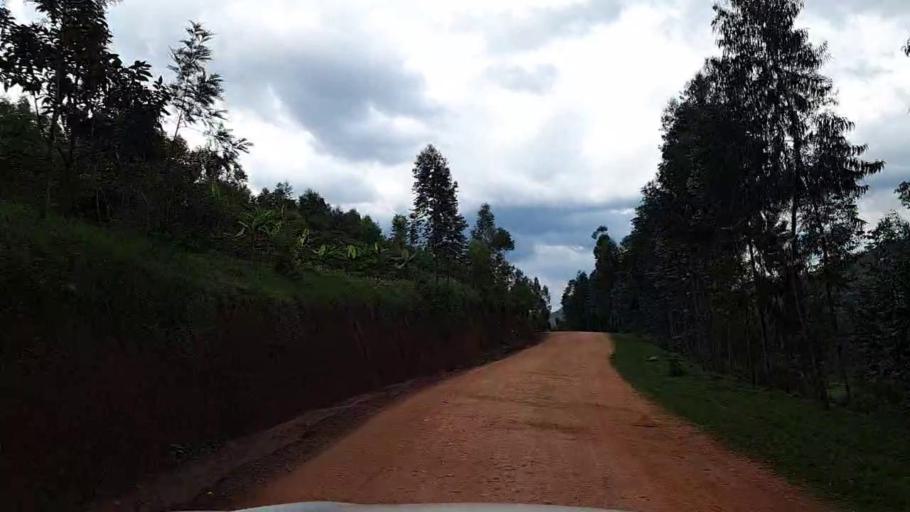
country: RW
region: Southern Province
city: Nyanza
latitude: -2.4060
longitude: 29.6754
